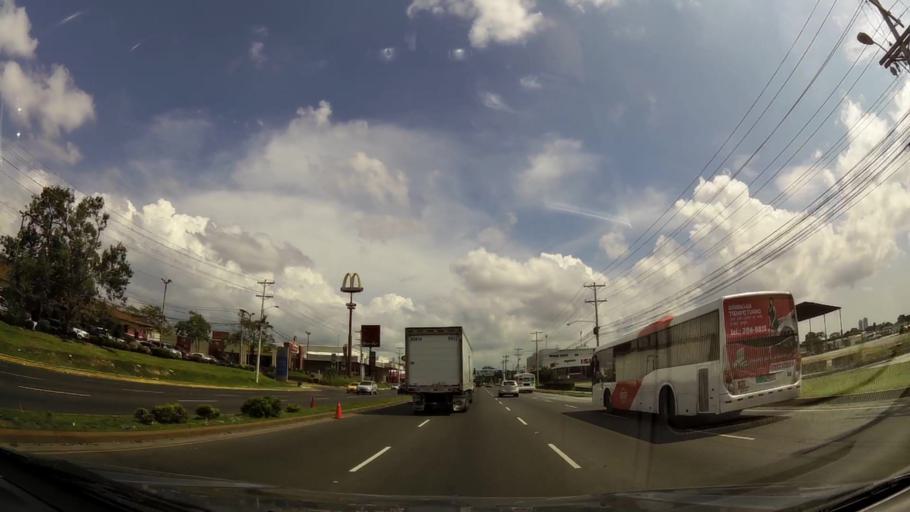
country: PA
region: Panama
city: San Miguelito
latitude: 9.0366
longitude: -79.4822
